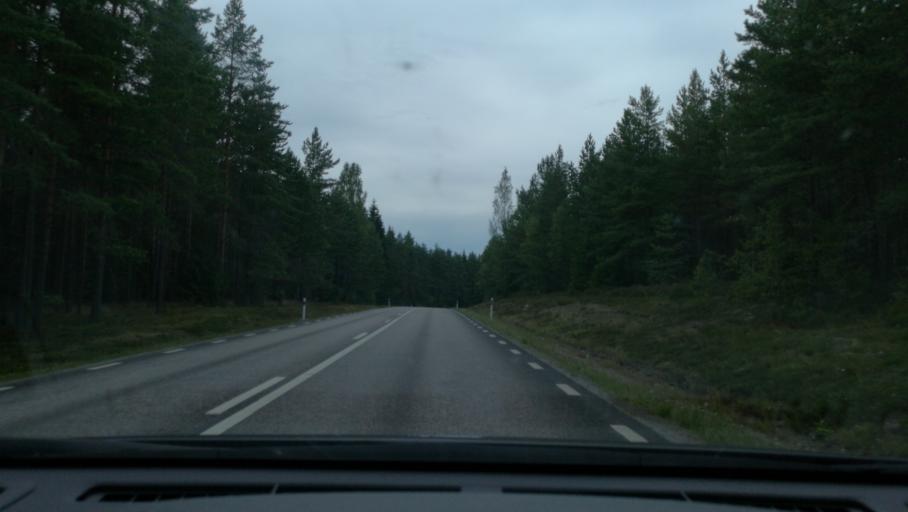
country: SE
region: Soedermanland
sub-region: Katrineholms Kommun
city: Katrineholm
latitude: 59.1045
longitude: 16.1801
